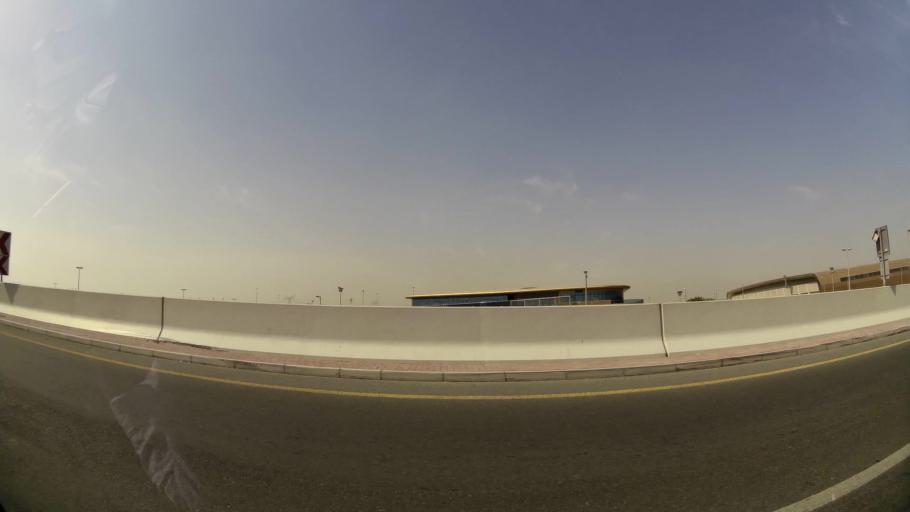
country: AE
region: Ash Shariqah
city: Sharjah
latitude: 25.2305
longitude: 55.4031
